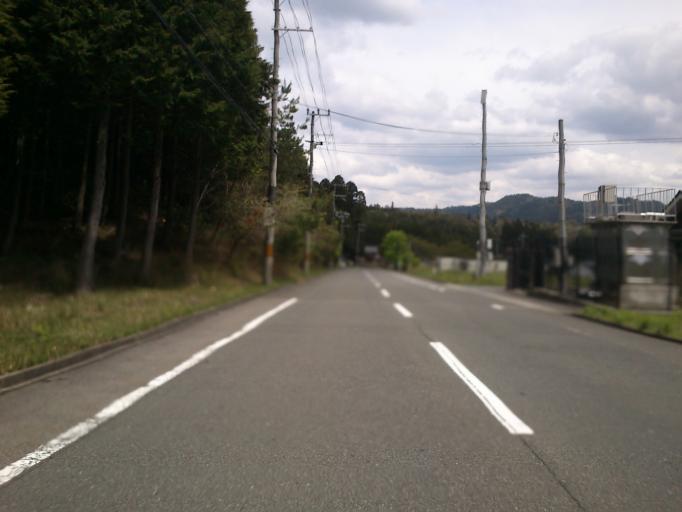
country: JP
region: Kyoto
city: Kameoka
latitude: 35.1991
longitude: 135.6312
